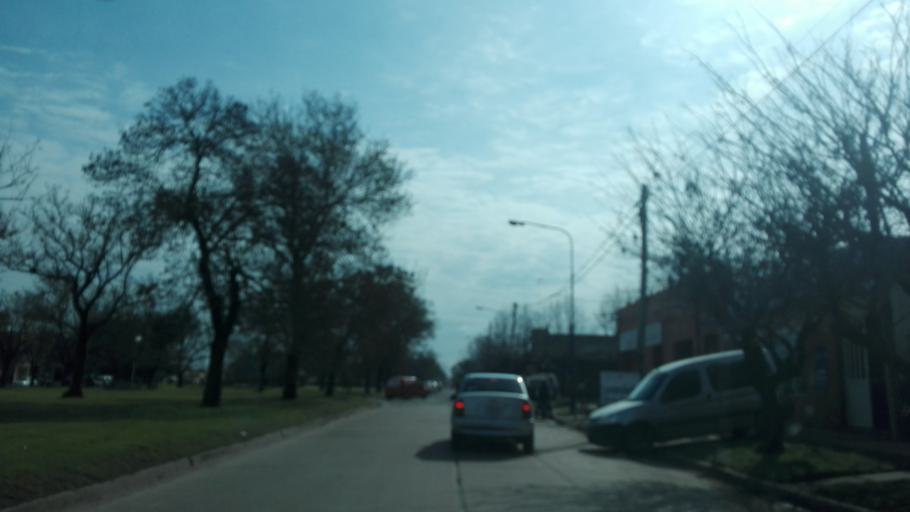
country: AR
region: Buenos Aires
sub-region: Partido de Chascomus
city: Chascomus
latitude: -35.5745
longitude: -58.0087
